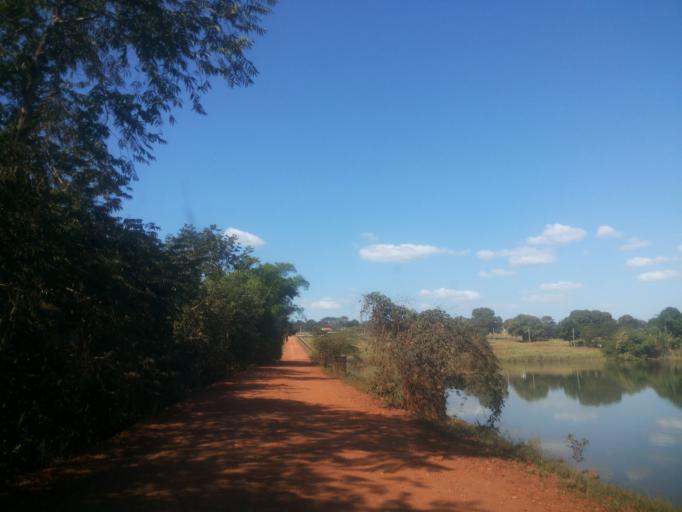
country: BR
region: Minas Gerais
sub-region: Santa Vitoria
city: Santa Vitoria
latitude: -19.0090
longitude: -50.4166
